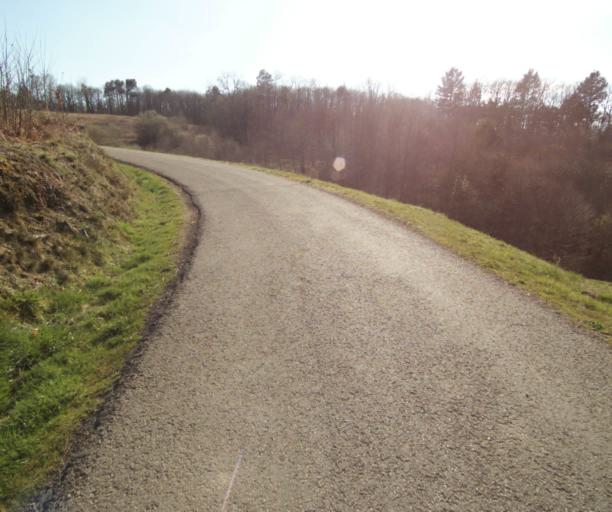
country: FR
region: Limousin
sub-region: Departement de la Correze
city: Saint-Mexant
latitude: 45.3197
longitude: 1.6191
